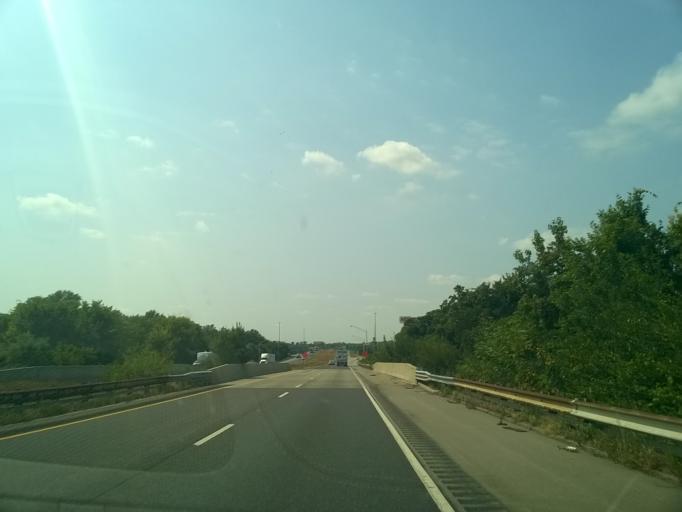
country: US
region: Indiana
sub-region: Vigo County
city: Terre Haute
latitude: 39.4311
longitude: -87.4074
